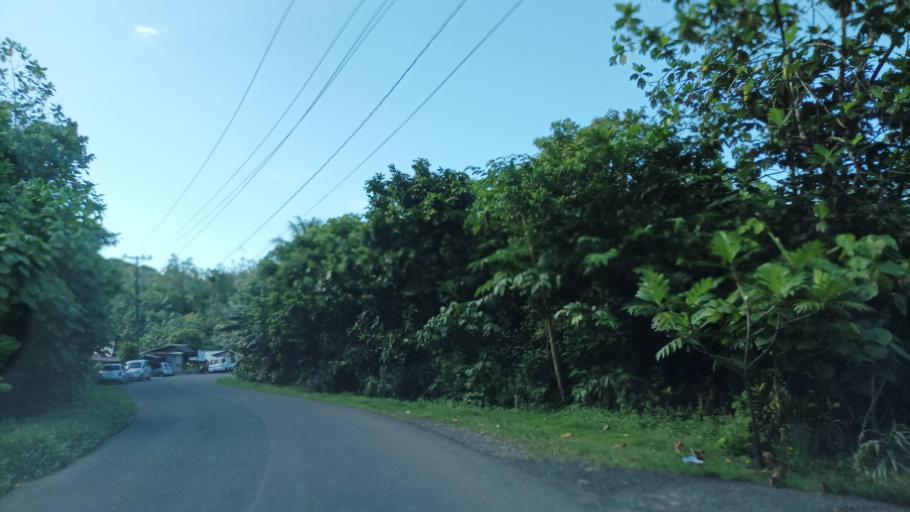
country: FM
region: Pohnpei
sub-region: Kolonia Municipality
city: Kolonia
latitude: 6.9337
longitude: 158.2779
